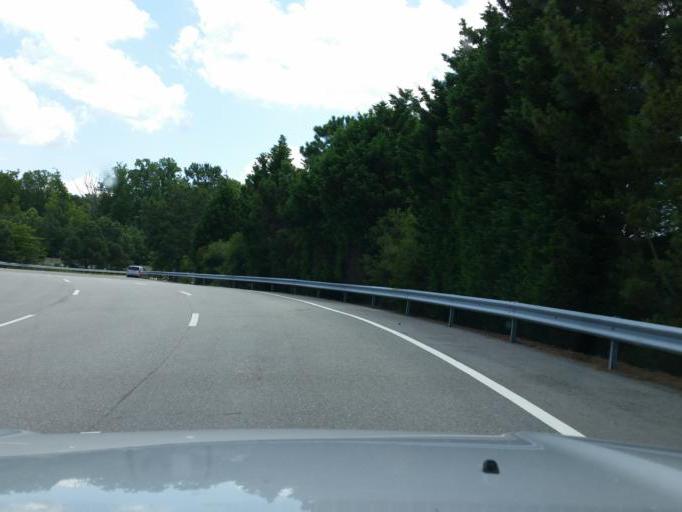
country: US
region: Virginia
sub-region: City of Williamsburg
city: Williamsburg
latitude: 37.2361
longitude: -76.6372
